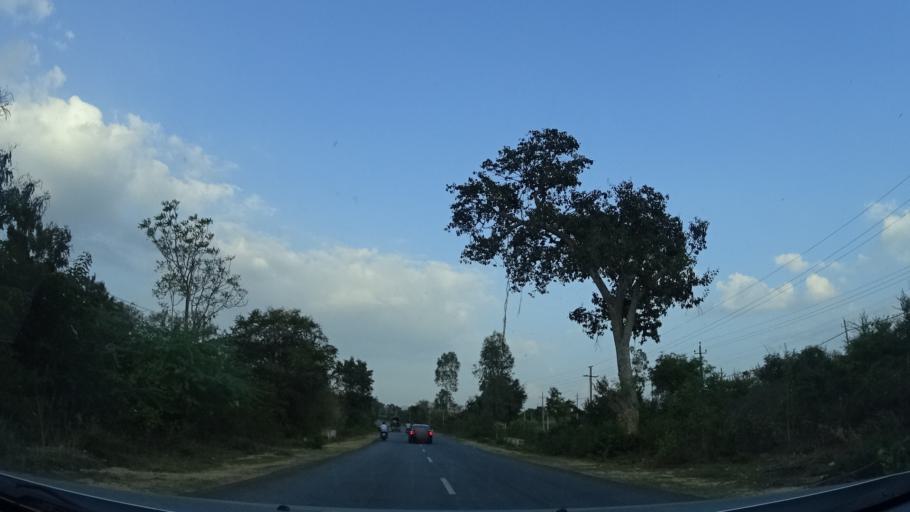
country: IN
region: Karnataka
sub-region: Ramanagara
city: Kanakapura
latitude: 12.4428
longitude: 77.2964
